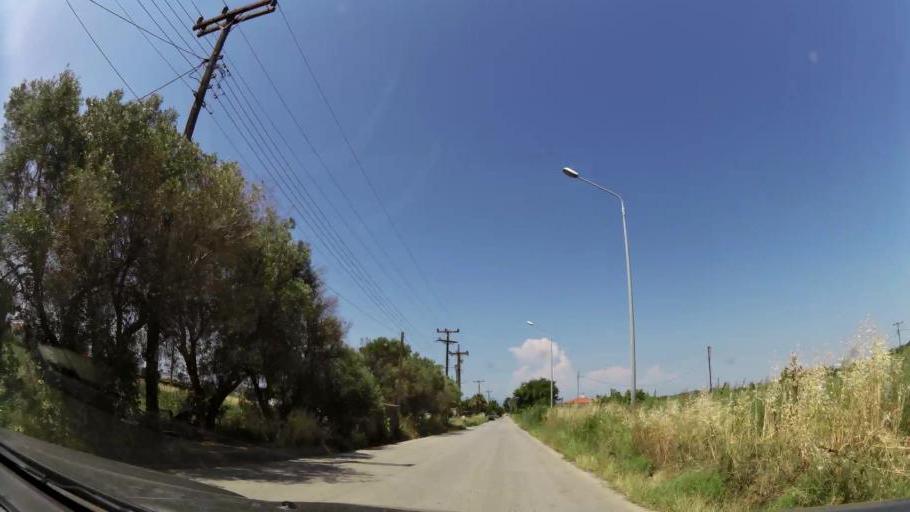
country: GR
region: Central Macedonia
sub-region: Nomos Thessalonikis
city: Agia Triada
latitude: 40.4954
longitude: 22.8304
